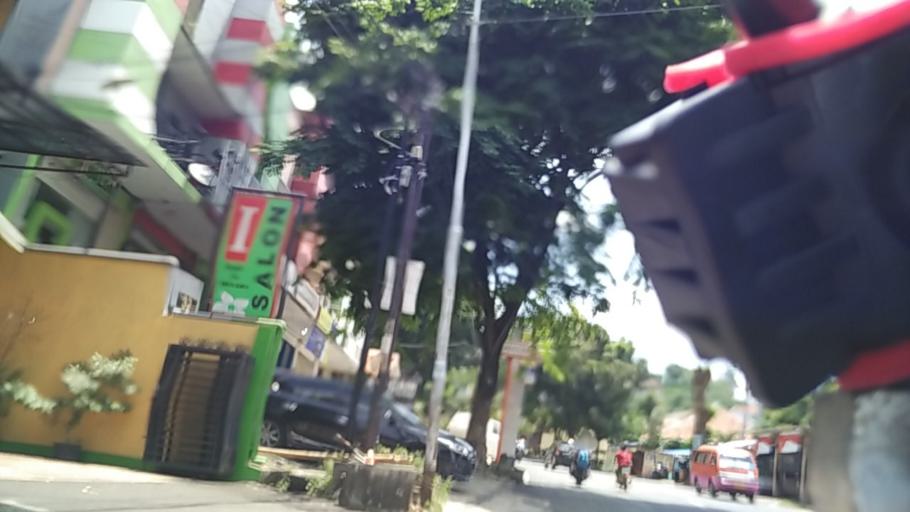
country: ID
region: Central Java
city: Semarang
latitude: -6.9994
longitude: 110.3788
